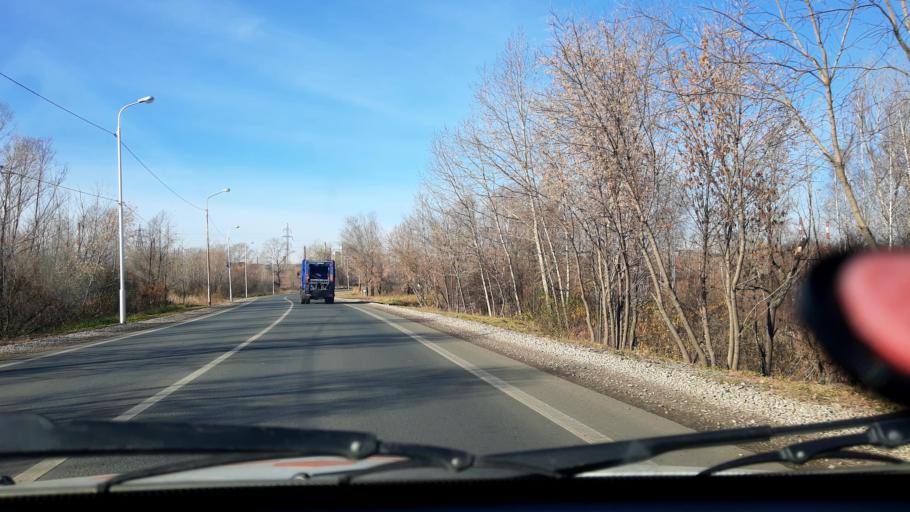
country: RU
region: Bashkortostan
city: Ufa
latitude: 54.8390
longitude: 56.1282
